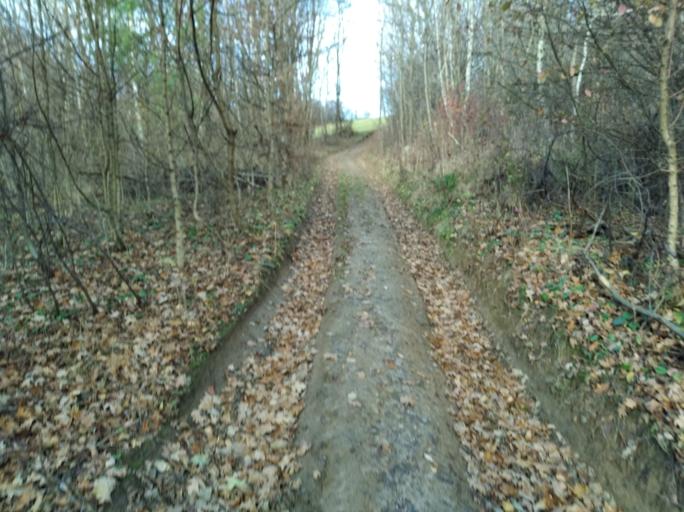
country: PL
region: Subcarpathian Voivodeship
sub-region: Powiat strzyzowski
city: Strzyzow
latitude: 49.8446
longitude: 21.8354
